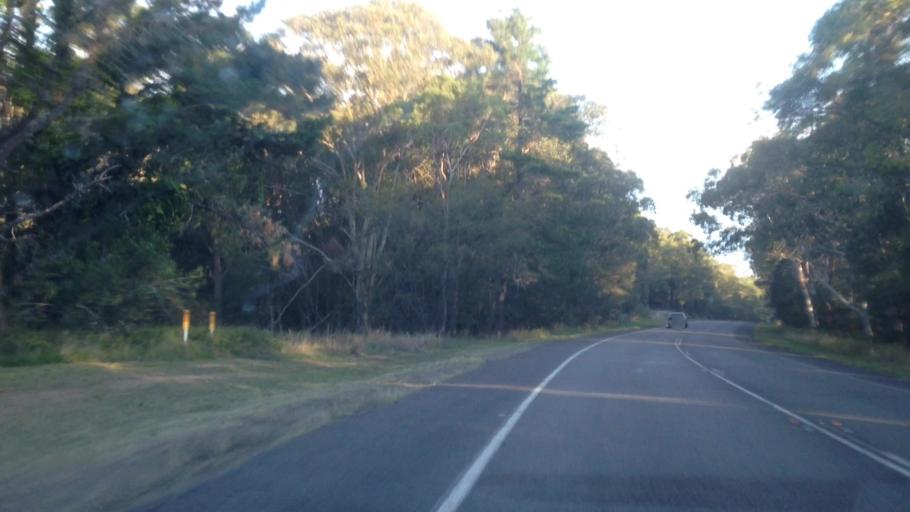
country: AU
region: New South Wales
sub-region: Lake Macquarie Shire
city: Cooranbong
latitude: -33.0552
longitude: 151.4739
